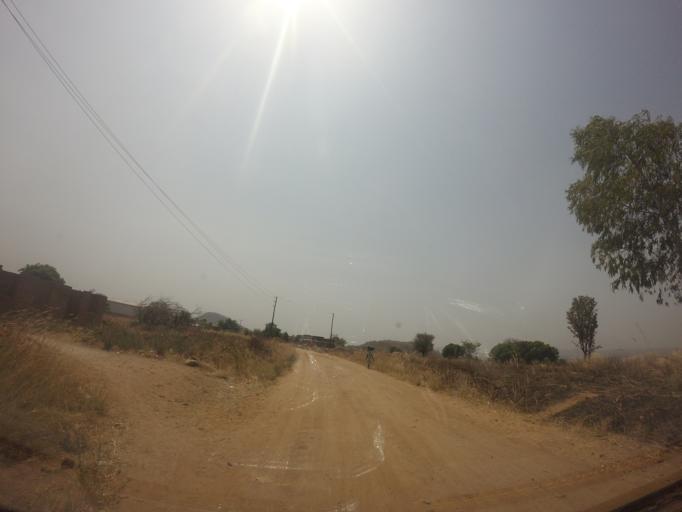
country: UG
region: Northern Region
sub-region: Arua District
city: Arua
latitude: 2.9373
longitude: 30.9814
